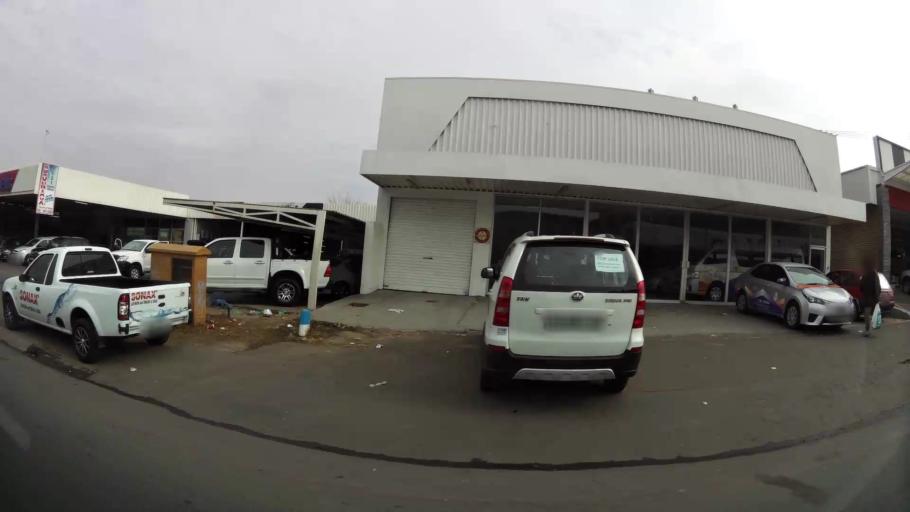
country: ZA
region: Orange Free State
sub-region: Mangaung Metropolitan Municipality
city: Bloemfontein
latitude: -29.1278
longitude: 26.2190
